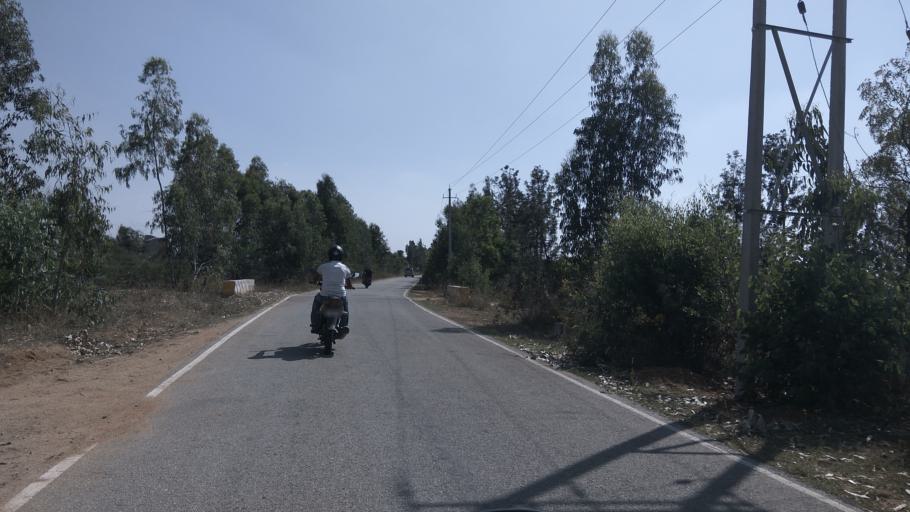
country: IN
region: Karnataka
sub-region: Kolar
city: Mulbagal
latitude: 13.1903
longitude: 78.3531
